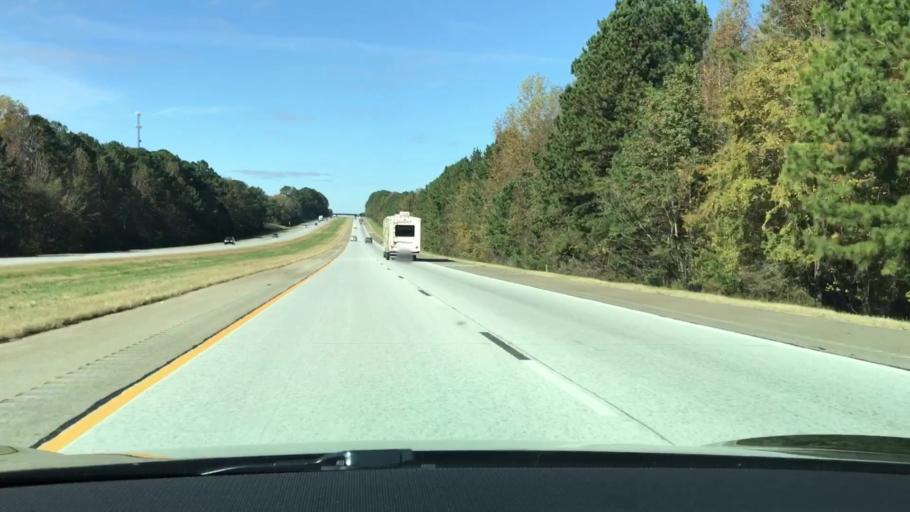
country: US
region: Georgia
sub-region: Putnam County
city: Jefferson
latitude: 33.5351
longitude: -83.2991
